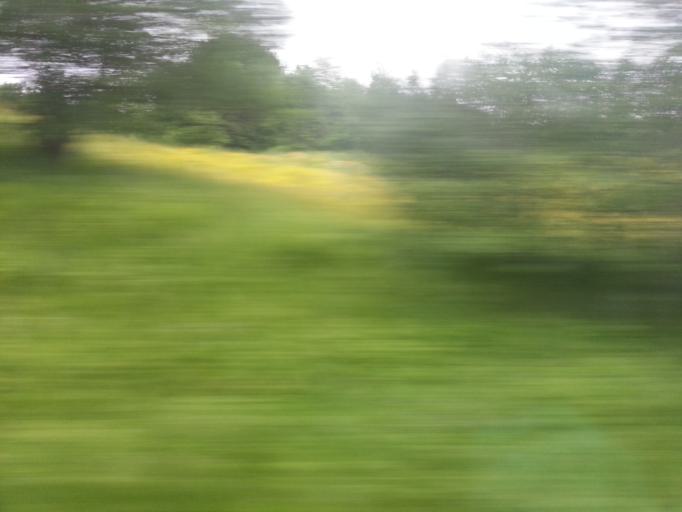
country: NO
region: Sor-Trondelag
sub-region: Melhus
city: Melhus
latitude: 63.3376
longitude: 10.3414
